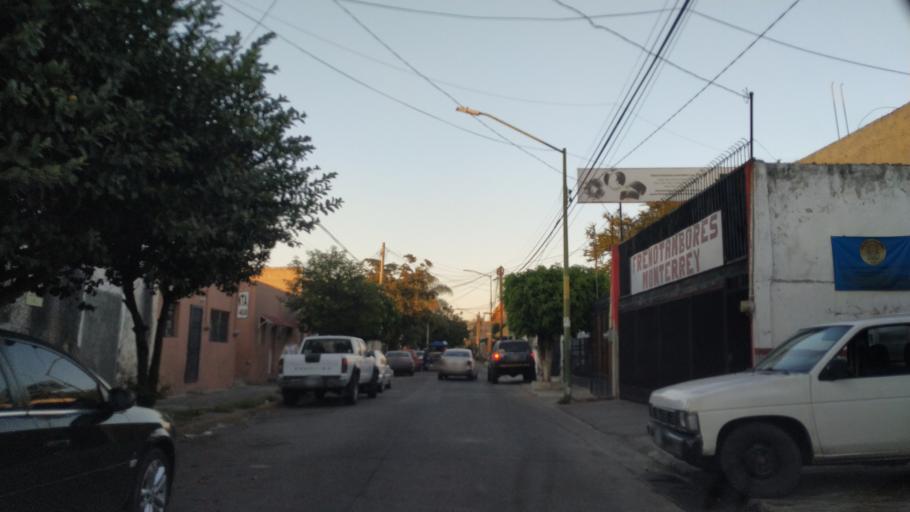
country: MX
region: Jalisco
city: Tlaquepaque
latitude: 20.6532
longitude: -103.3356
